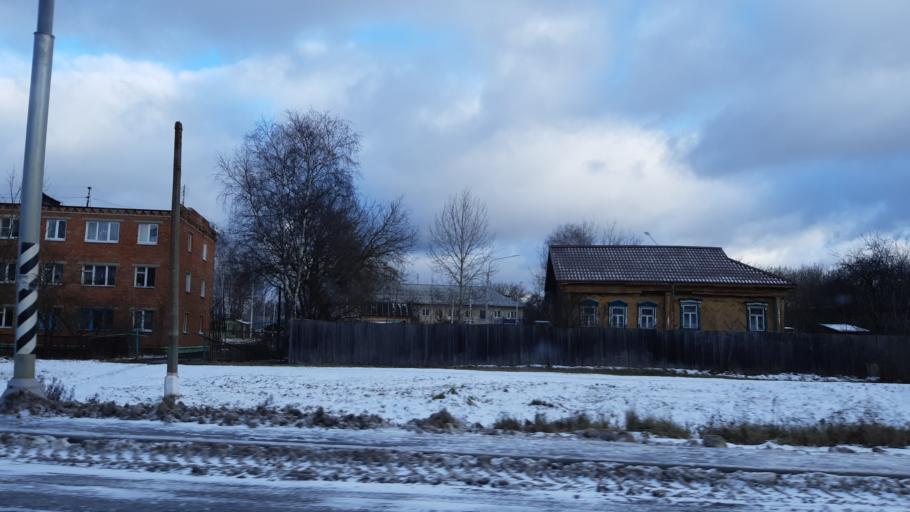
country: RU
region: Moskovskaya
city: Noginsk-9
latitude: 55.9496
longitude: 38.5533
